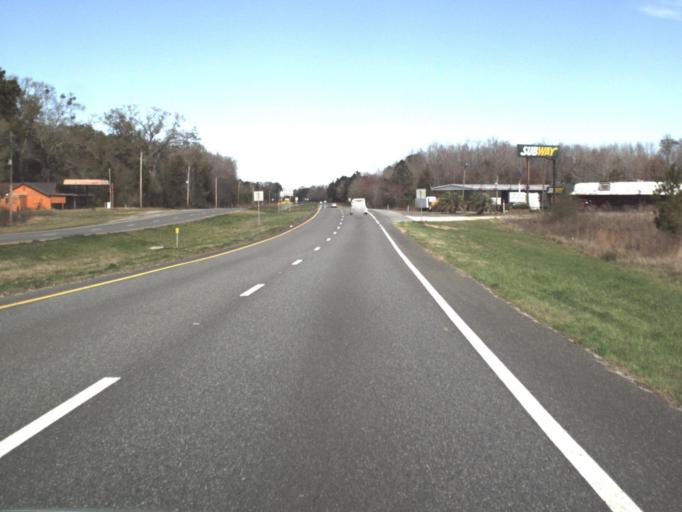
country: US
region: Florida
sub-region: Jackson County
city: Marianna
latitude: 30.7597
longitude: -85.3787
